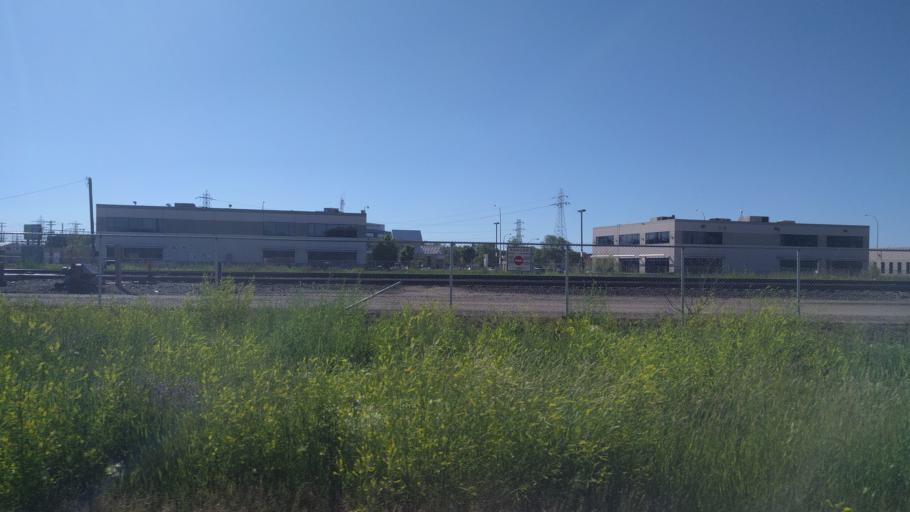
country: CA
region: Manitoba
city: Winnipeg
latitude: 49.8550
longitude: -97.1509
